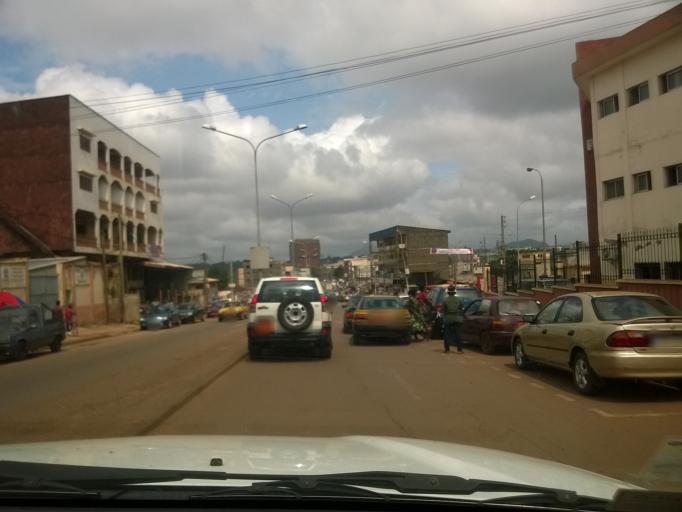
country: CM
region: Centre
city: Yaounde
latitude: 3.8635
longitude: 11.5273
